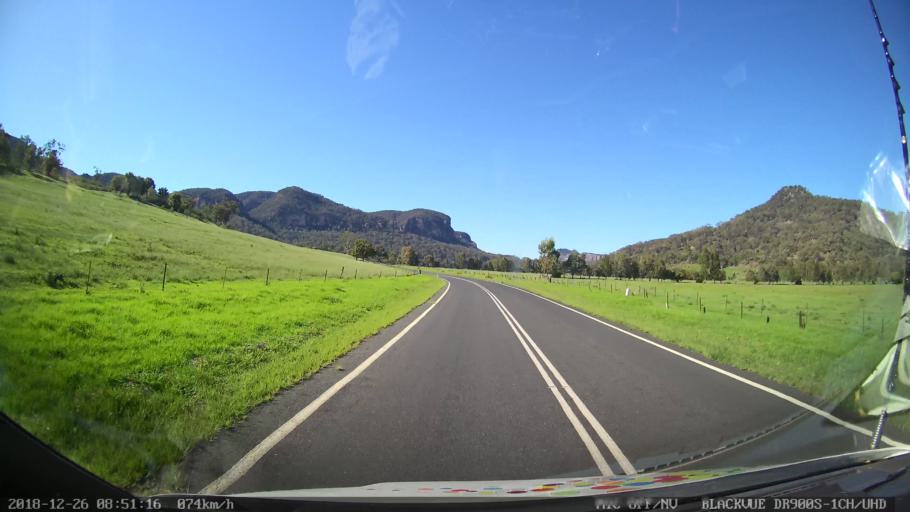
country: AU
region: New South Wales
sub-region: Mid-Western Regional
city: Kandos
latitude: -32.5833
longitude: 150.0894
